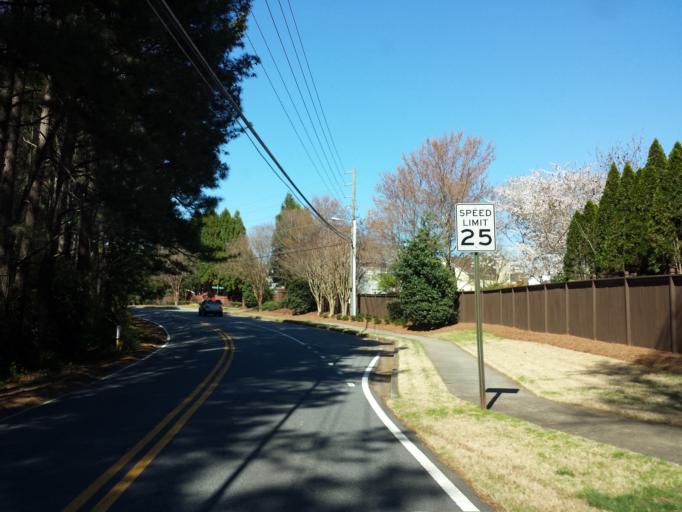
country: US
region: Georgia
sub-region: Cobb County
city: Smyrna
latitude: 33.9346
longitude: -84.4808
